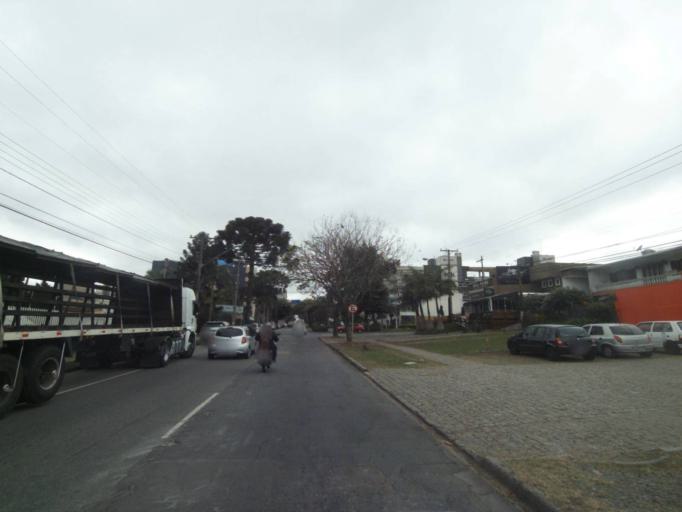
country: BR
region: Parana
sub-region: Curitiba
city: Curitiba
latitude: -25.4507
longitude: -49.2968
